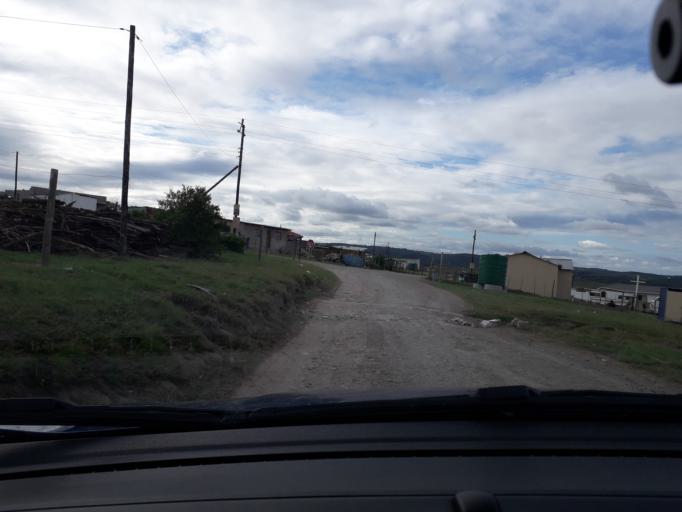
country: ZA
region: Eastern Cape
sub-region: Buffalo City Metropolitan Municipality
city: East London
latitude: -32.8526
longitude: 27.9845
